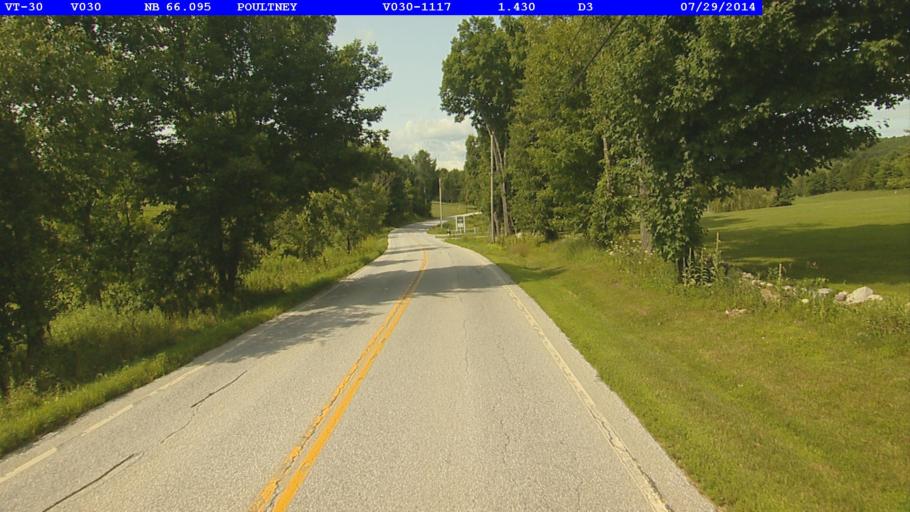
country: US
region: Vermont
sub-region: Rutland County
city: Poultney
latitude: 43.4840
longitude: -73.2028
